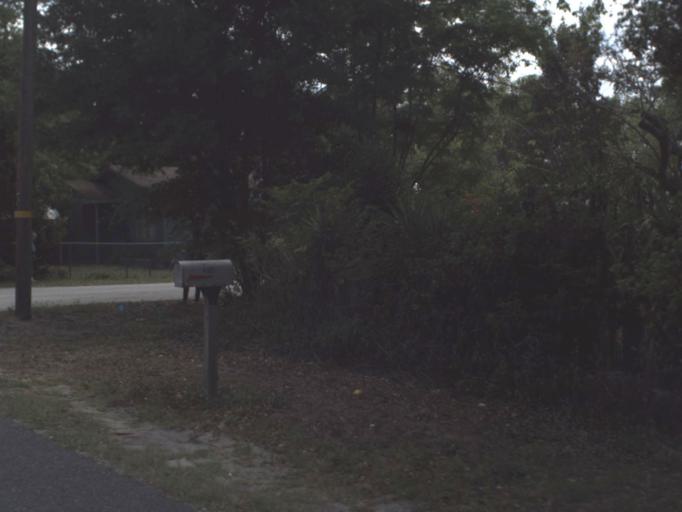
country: US
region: Florida
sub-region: Lake County
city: Groveland
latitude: 28.5644
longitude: -81.8556
